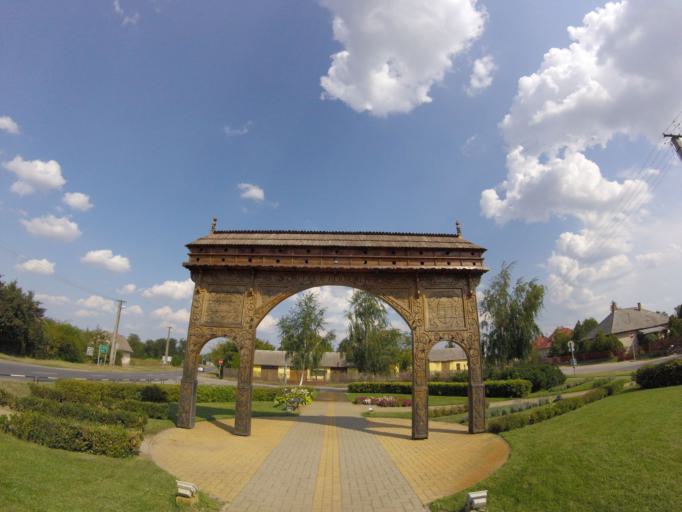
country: HU
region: Szabolcs-Szatmar-Bereg
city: Nyirbogdany
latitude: 48.0582
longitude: 21.9384
